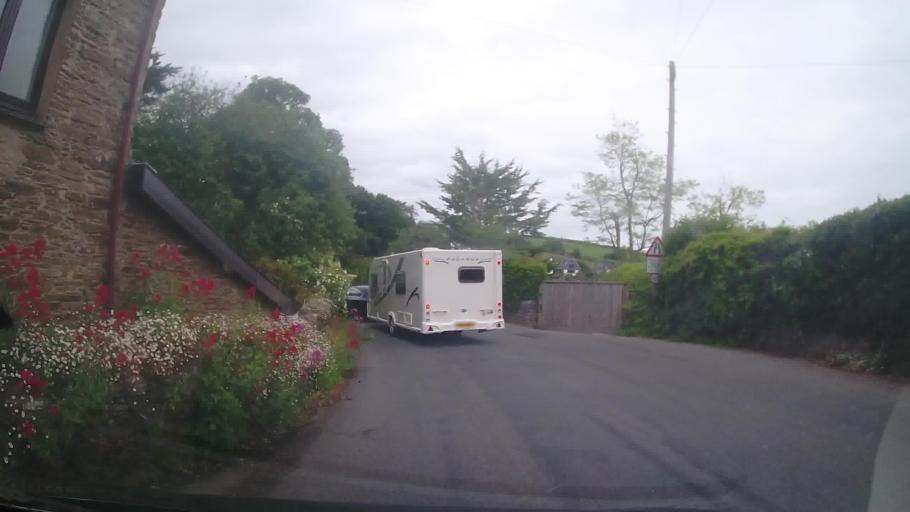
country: GB
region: England
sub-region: Devon
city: Kingsbridge
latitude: 50.2745
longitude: -3.7616
